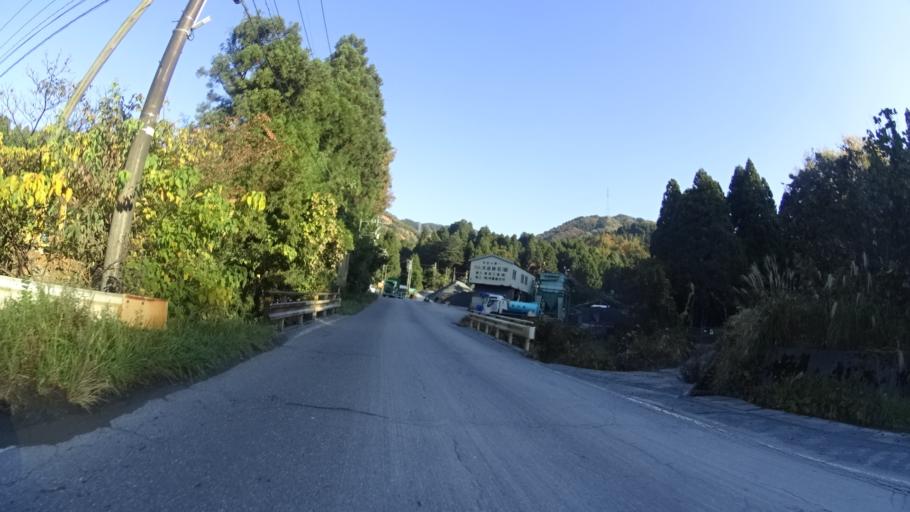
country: JP
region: Fukui
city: Maruoka
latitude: 36.1126
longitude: 136.3194
